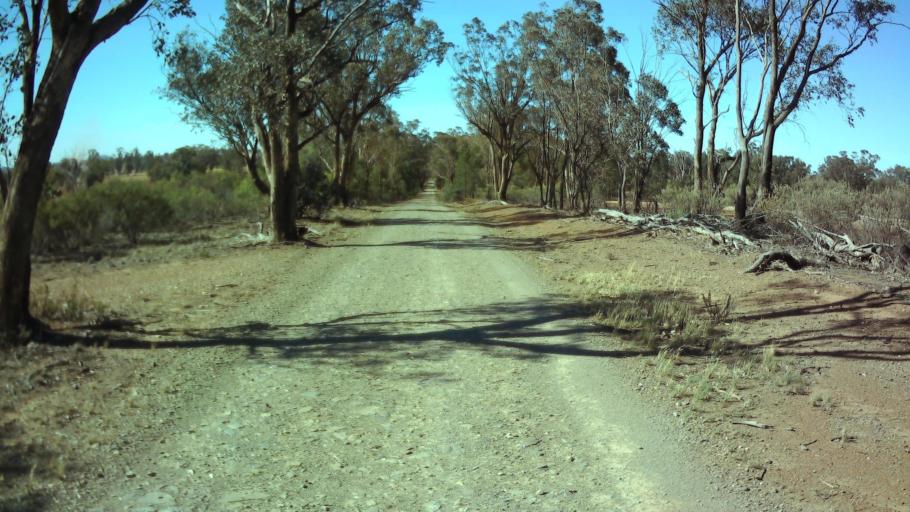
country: AU
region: New South Wales
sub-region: Weddin
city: Grenfell
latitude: -33.7470
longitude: 147.8307
